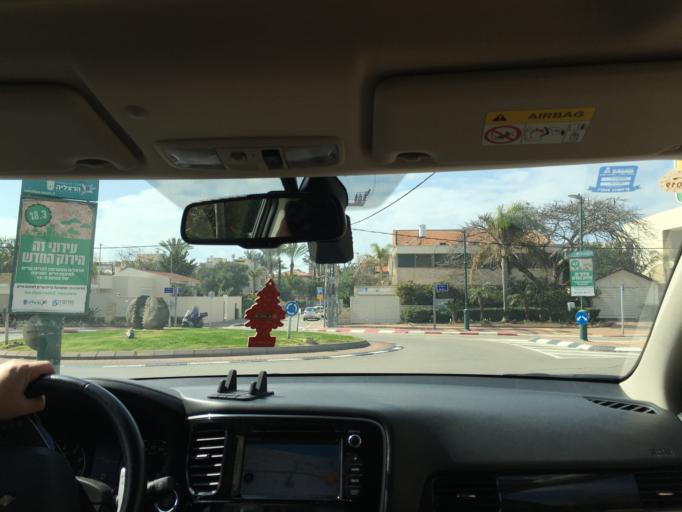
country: IL
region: Tel Aviv
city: Herzliya Pituah
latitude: 32.1814
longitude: 34.8074
